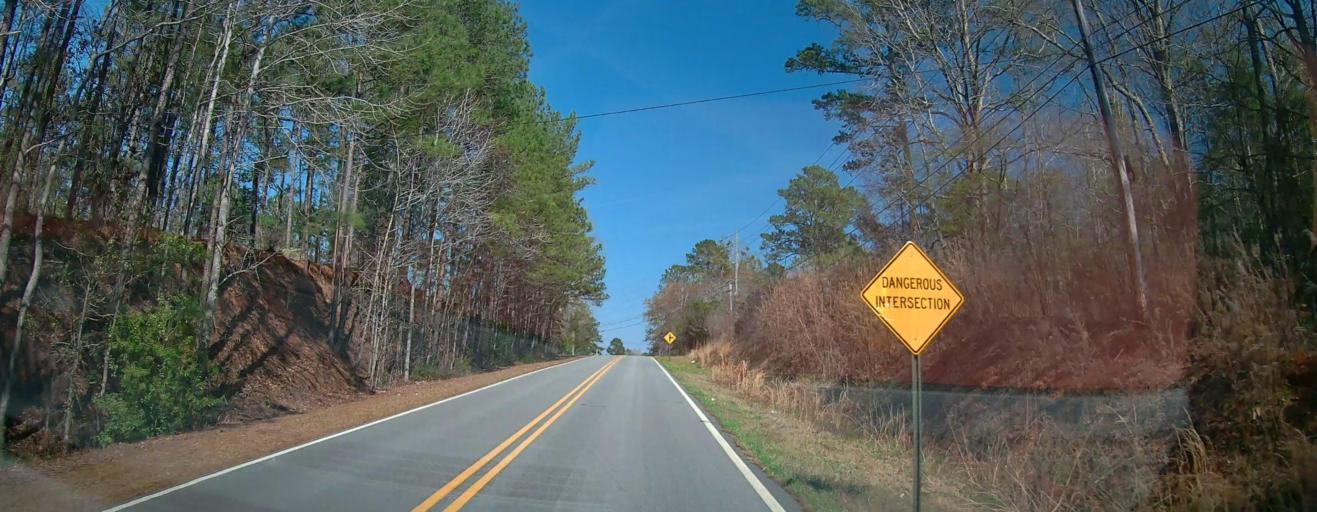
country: US
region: Georgia
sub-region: Bibb County
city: Macon
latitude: 32.9030
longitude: -83.6308
